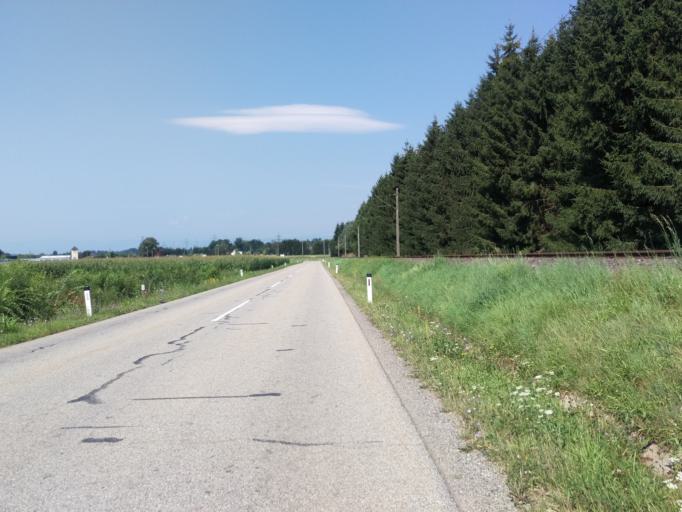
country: AT
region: Styria
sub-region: Politischer Bezirk Graz-Umgebung
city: Werndorf
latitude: 46.9048
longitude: 15.4873
